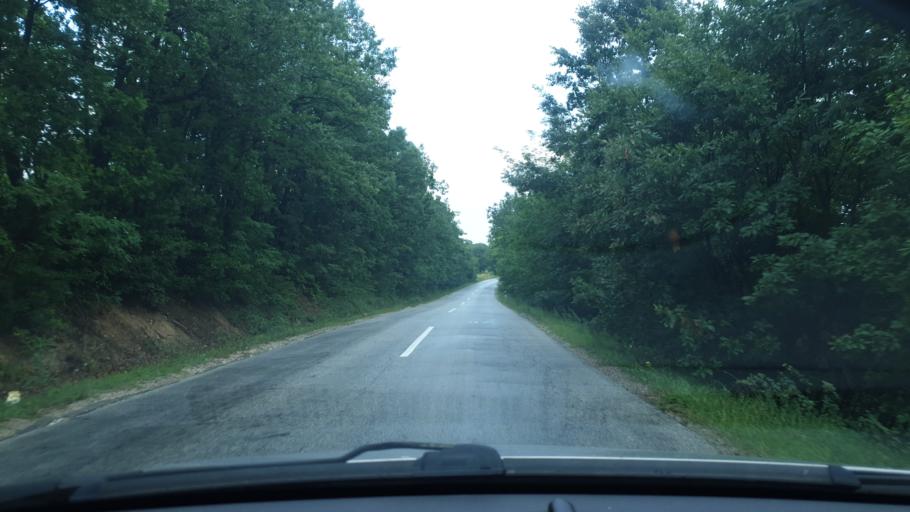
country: RS
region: Central Serbia
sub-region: Sumadijski Okrug
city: Kragujevac
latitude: 44.0508
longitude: 20.7837
